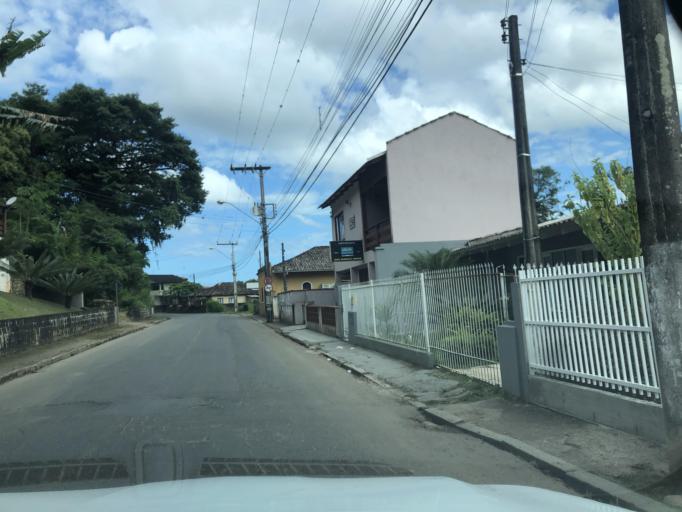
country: BR
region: Santa Catarina
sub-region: Sao Francisco Do Sul
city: Sao Francisco do Sul
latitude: -26.2437
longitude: -48.6340
